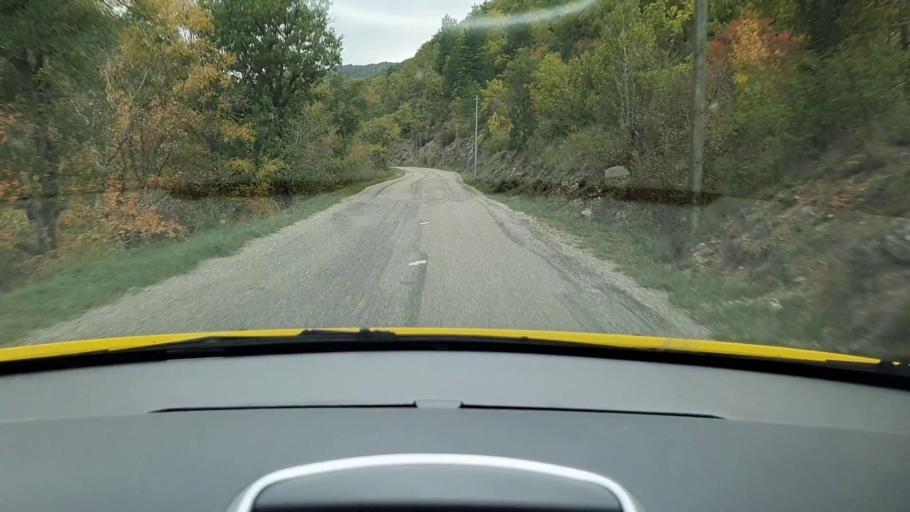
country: FR
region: Languedoc-Roussillon
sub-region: Departement de la Lozere
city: Meyrueis
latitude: 44.0762
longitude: 3.3620
